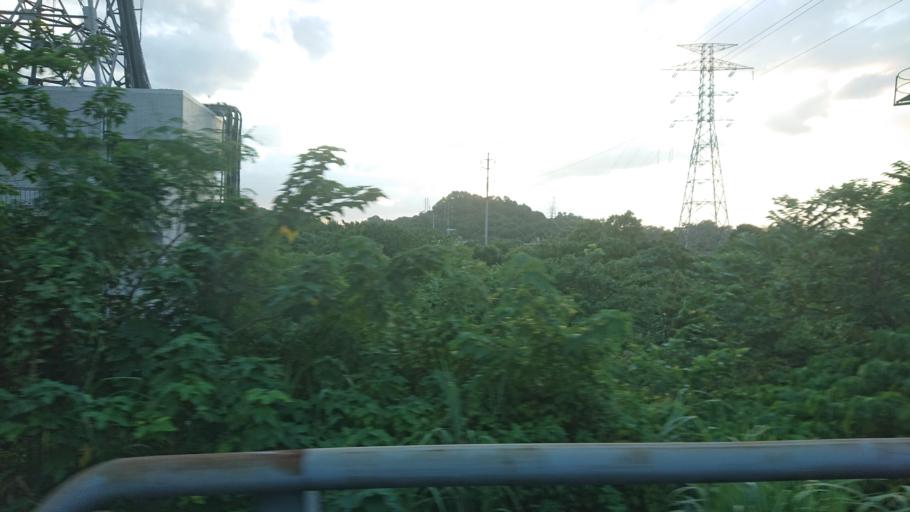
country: TW
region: Taipei
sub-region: Taipei
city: Banqiao
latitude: 24.9903
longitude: 121.4861
